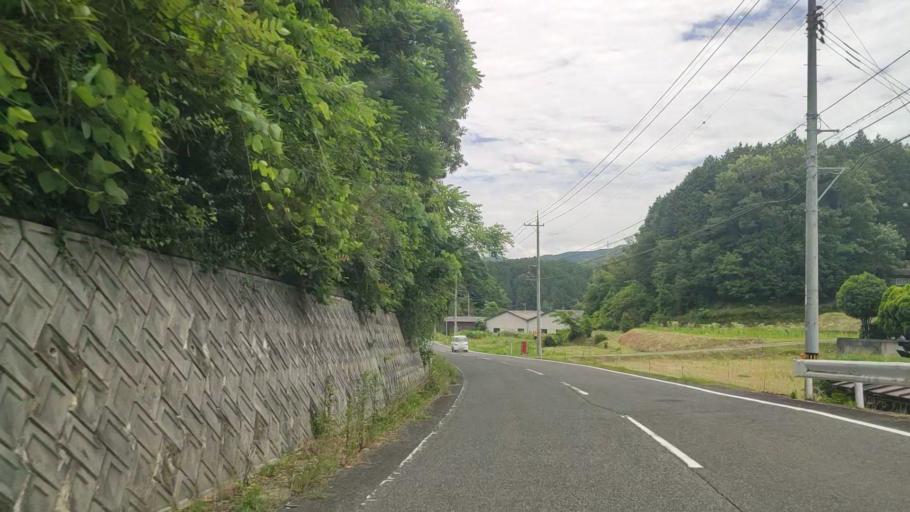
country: JP
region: Hyogo
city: Yamazakicho-nakabirose
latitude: 35.0952
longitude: 134.2920
